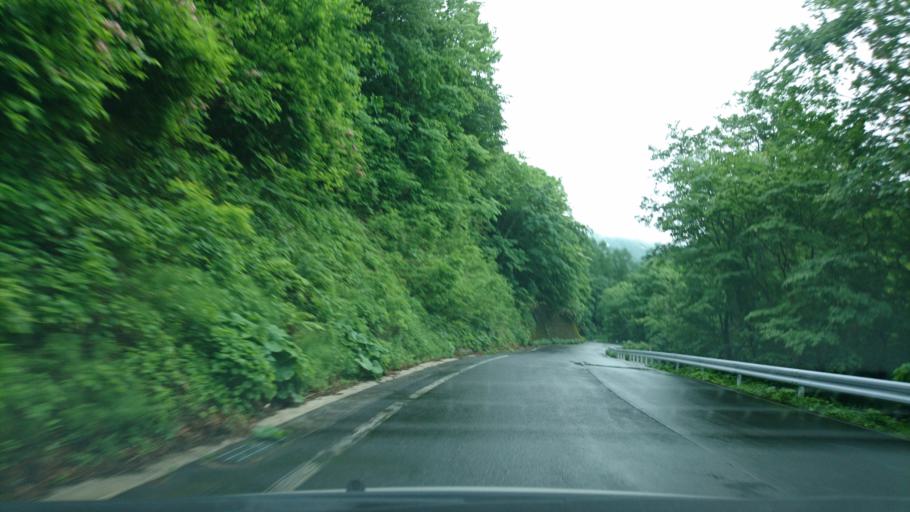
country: JP
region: Iwate
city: Ichinoseki
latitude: 39.0005
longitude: 140.8349
